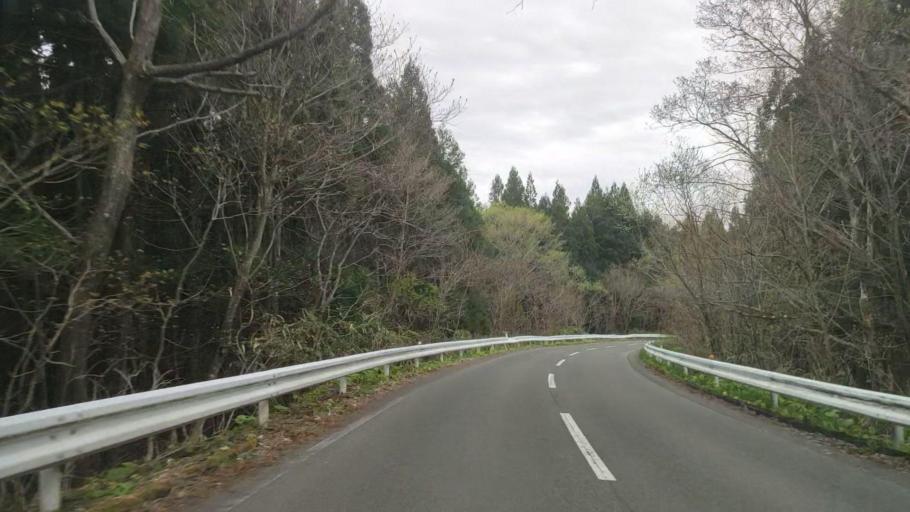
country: JP
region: Akita
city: Hanawa
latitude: 40.3977
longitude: 140.8003
